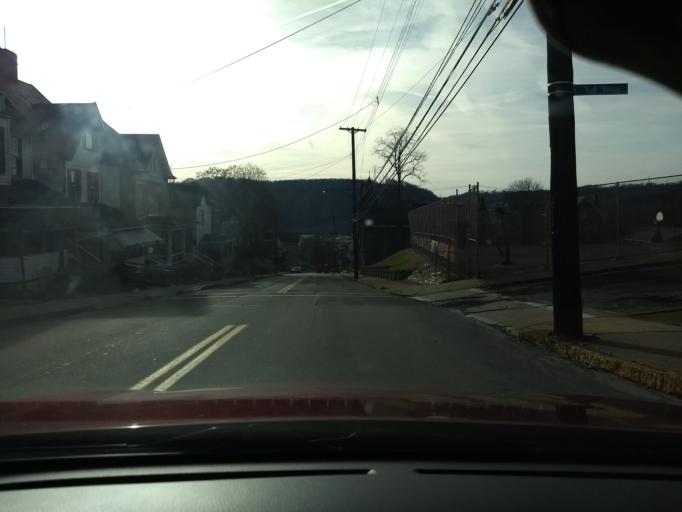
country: US
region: Pennsylvania
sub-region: Allegheny County
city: Homestead
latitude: 40.4123
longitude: -79.9409
